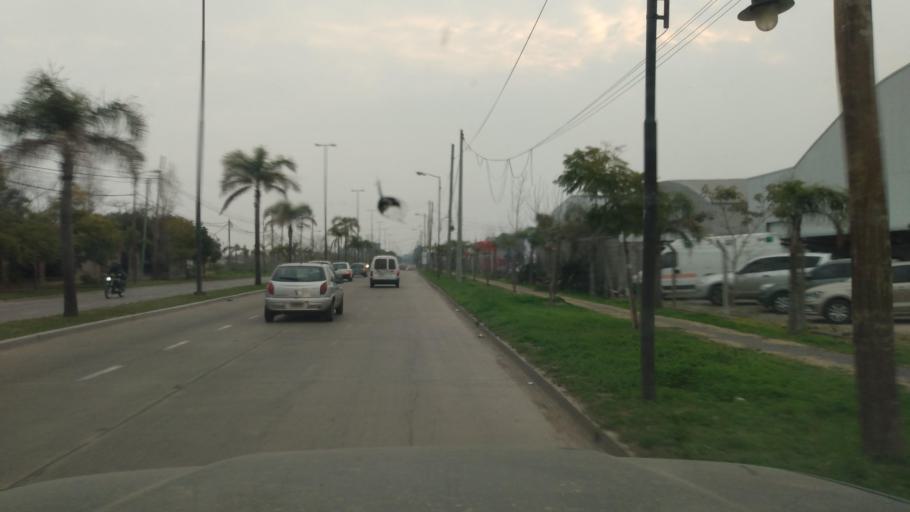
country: AR
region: Buenos Aires
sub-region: Partido de Tigre
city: Tigre
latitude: -34.4573
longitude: -58.5859
